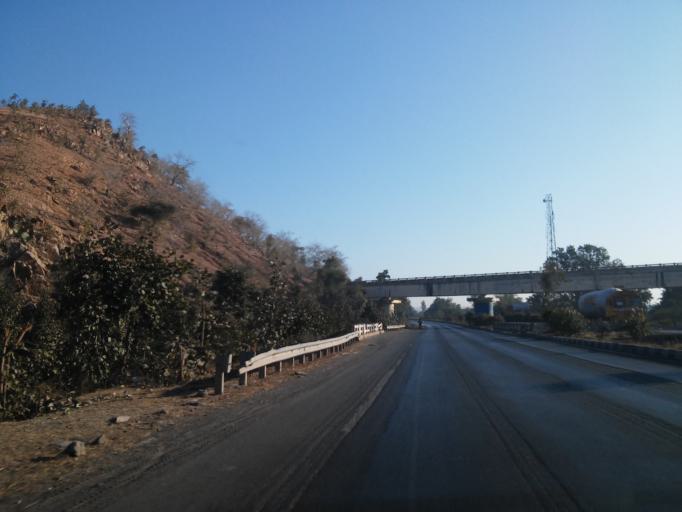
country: IN
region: Rajasthan
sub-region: Dungarpur
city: Dungarpur
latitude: 24.0029
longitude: 73.6524
